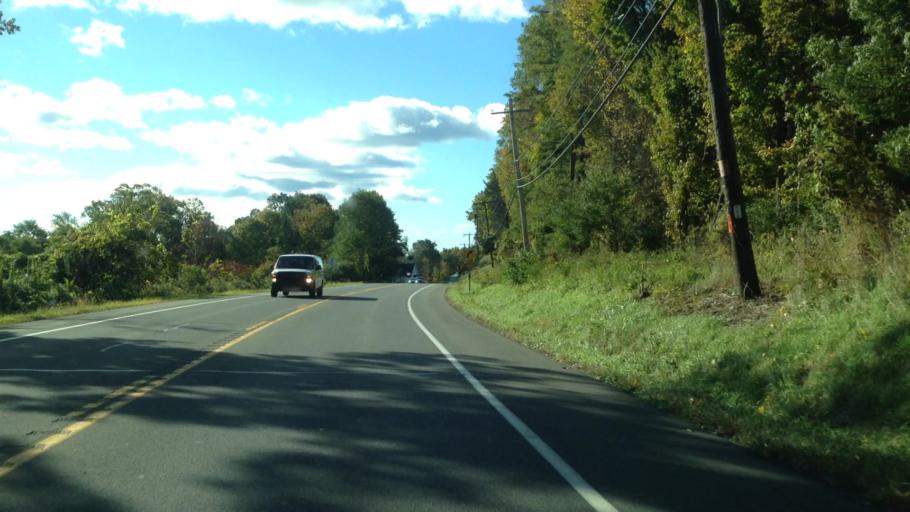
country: US
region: New York
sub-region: Dutchess County
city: Hyde Park
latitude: 41.8355
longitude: -73.9650
